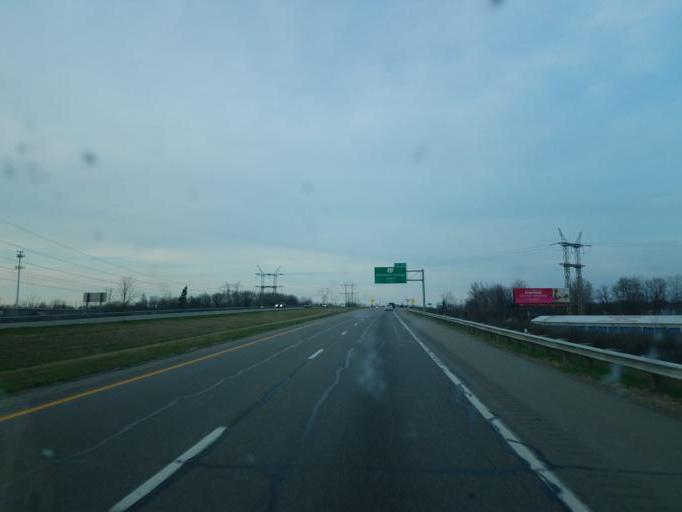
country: US
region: Ohio
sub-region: Lorain County
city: Avon
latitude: 41.4503
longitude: -82.0699
